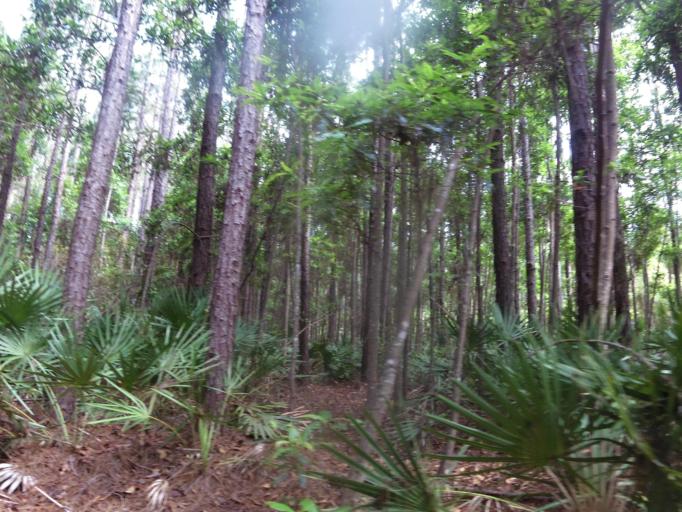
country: US
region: Florida
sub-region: Duval County
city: Atlantic Beach
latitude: 30.4558
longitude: -81.4753
